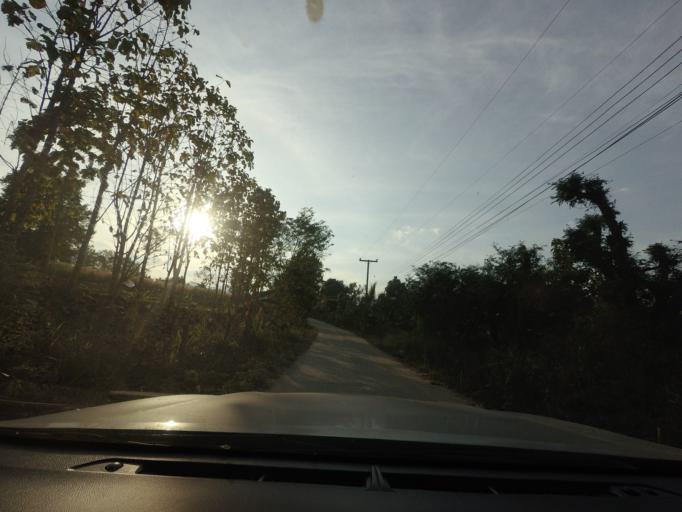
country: TH
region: Mae Hong Son
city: Mae Hi
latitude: 19.3413
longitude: 98.4300
